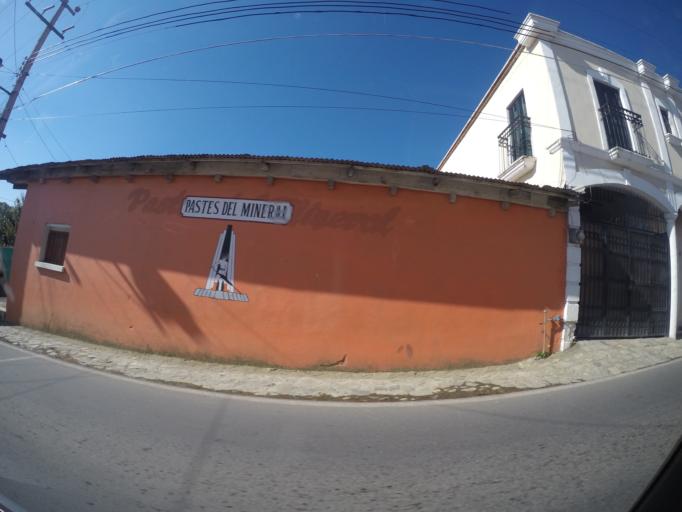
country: MX
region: Hidalgo
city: Mineral del Monte
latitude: 20.1353
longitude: -98.6756
